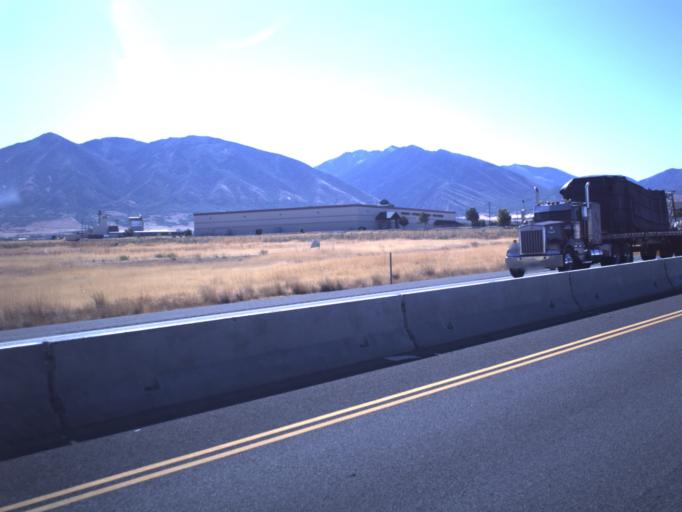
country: US
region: Utah
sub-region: Tooele County
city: Erda
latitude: 40.5778
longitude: -112.2943
